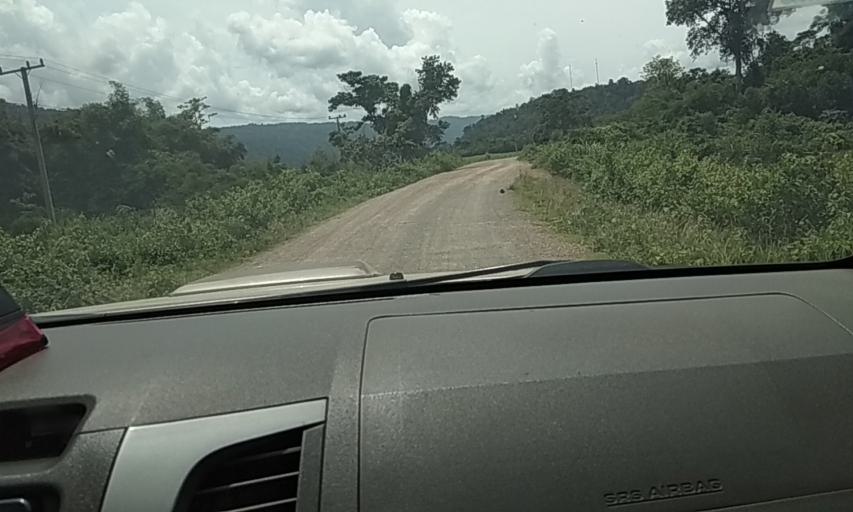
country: LA
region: Bolikhamxai
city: Ban Nahin
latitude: 18.1514
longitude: 104.7322
